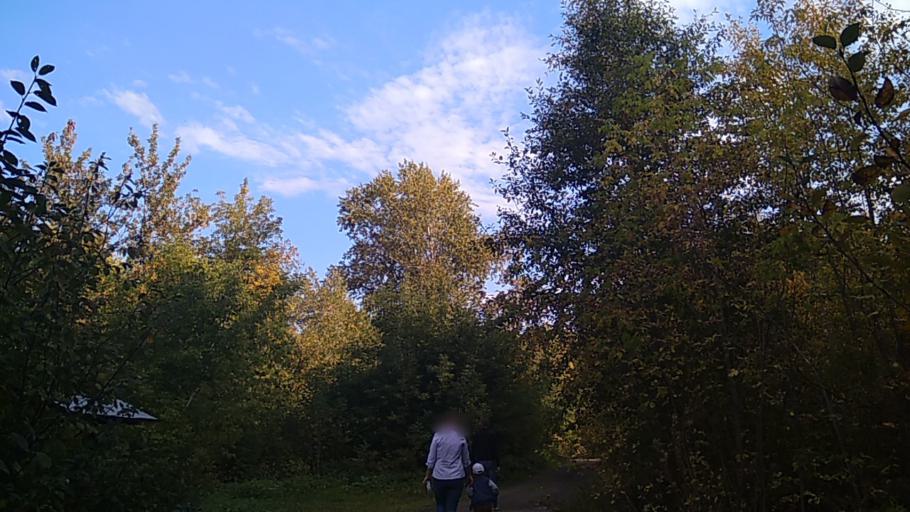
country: RU
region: Sverdlovsk
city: Pokrovskoye
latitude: 56.4337
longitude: 61.5952
